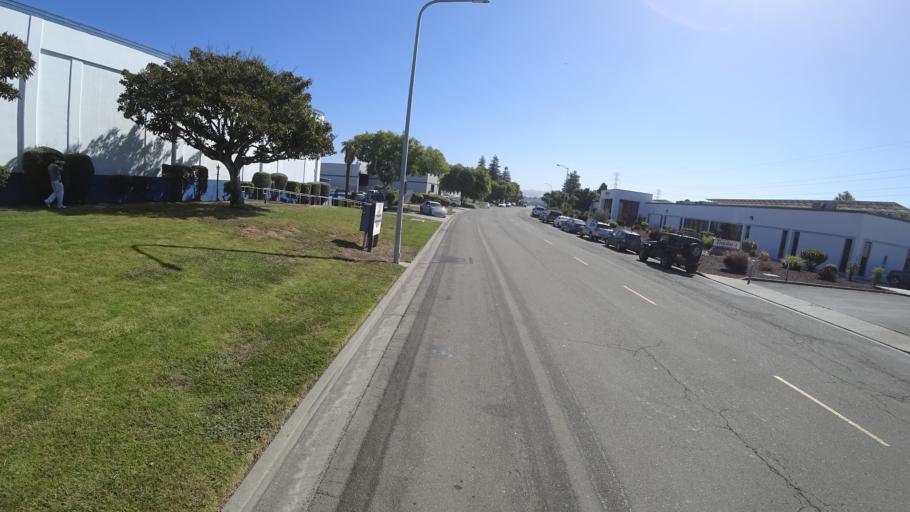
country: US
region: California
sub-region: Alameda County
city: Cherryland
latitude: 37.6274
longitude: -122.1158
